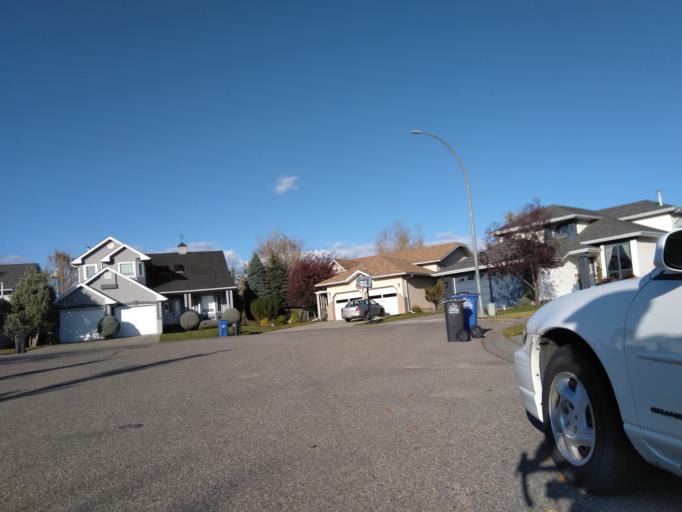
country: CA
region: Alberta
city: Cochrane
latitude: 51.1789
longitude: -114.4710
